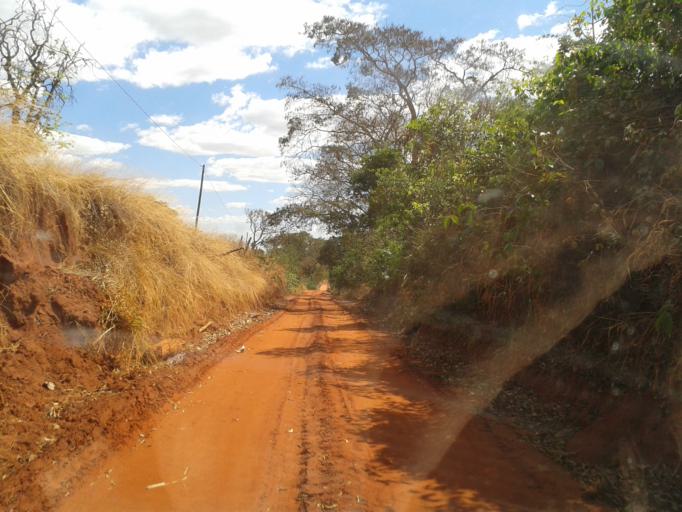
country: BR
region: Minas Gerais
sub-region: Centralina
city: Centralina
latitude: -18.7768
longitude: -49.0849
